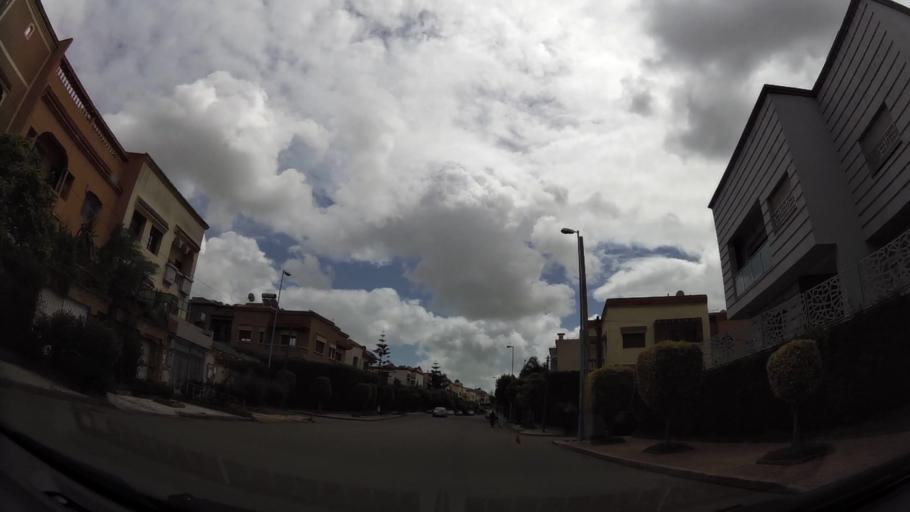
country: MA
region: Grand Casablanca
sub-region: Casablanca
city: Casablanca
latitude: 33.5339
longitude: -7.6027
